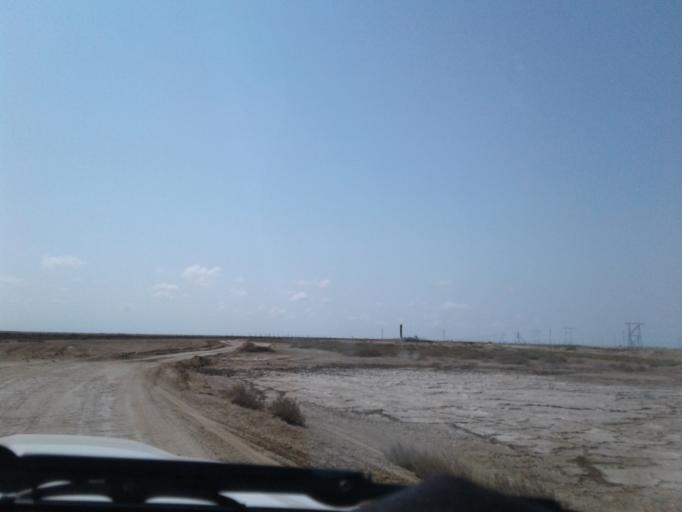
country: IR
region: Golestan
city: Gomishan
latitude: 37.8227
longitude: 53.9216
